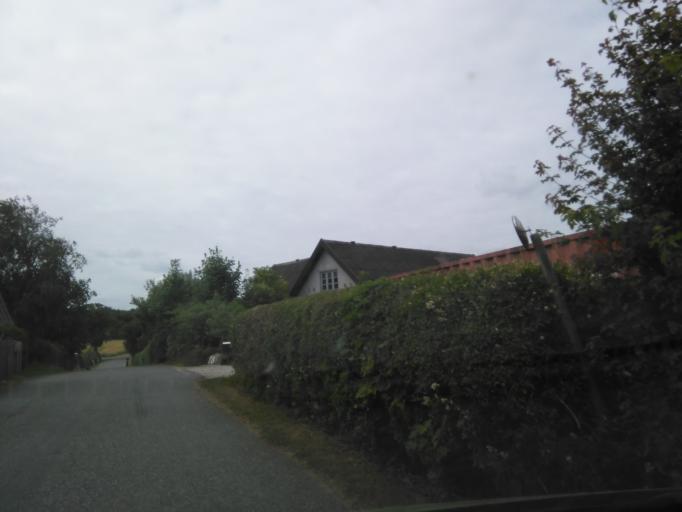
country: DK
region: Central Jutland
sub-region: Arhus Kommune
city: Solbjerg
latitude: 56.0162
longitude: 10.0707
